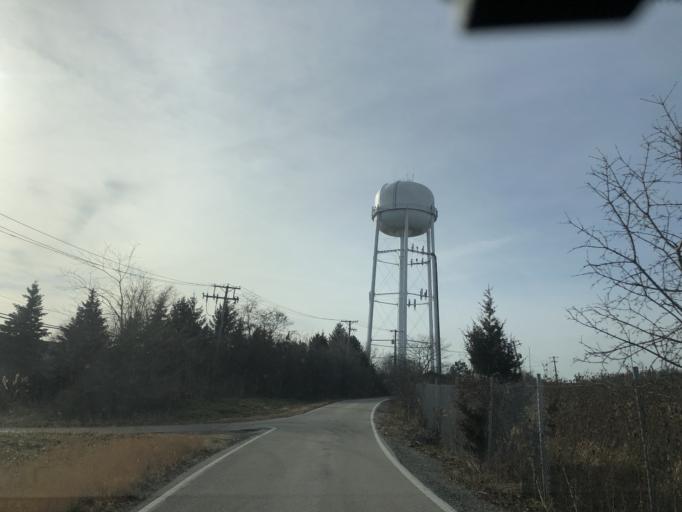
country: US
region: Illinois
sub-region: Cook County
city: Lemont
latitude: 41.7020
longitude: -88.0276
